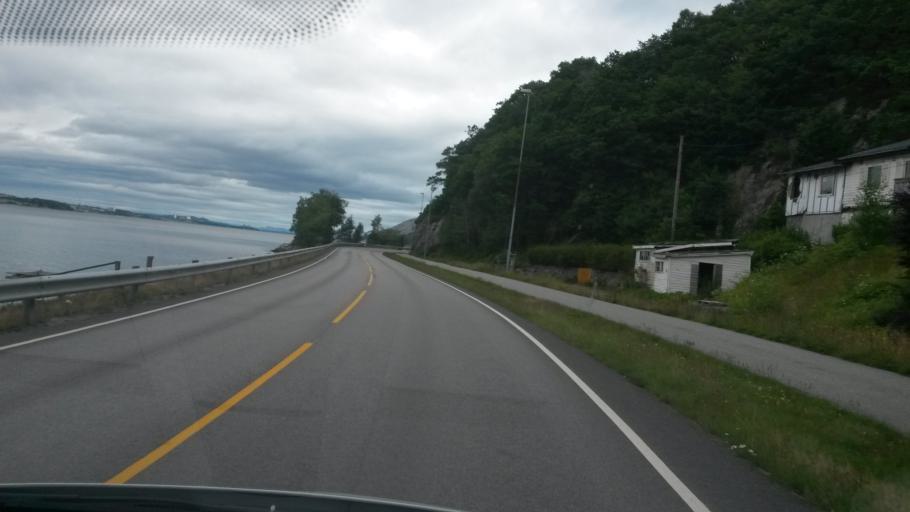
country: NO
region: Rogaland
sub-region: Sandnes
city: Sandnes
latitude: 58.8681
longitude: 5.7603
